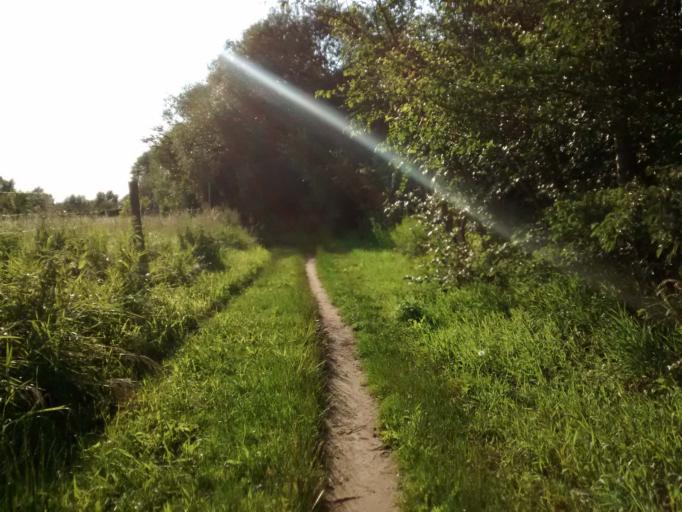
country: DE
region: Brandenburg
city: Hohen Neuendorf
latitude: 52.6547
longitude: 13.2638
